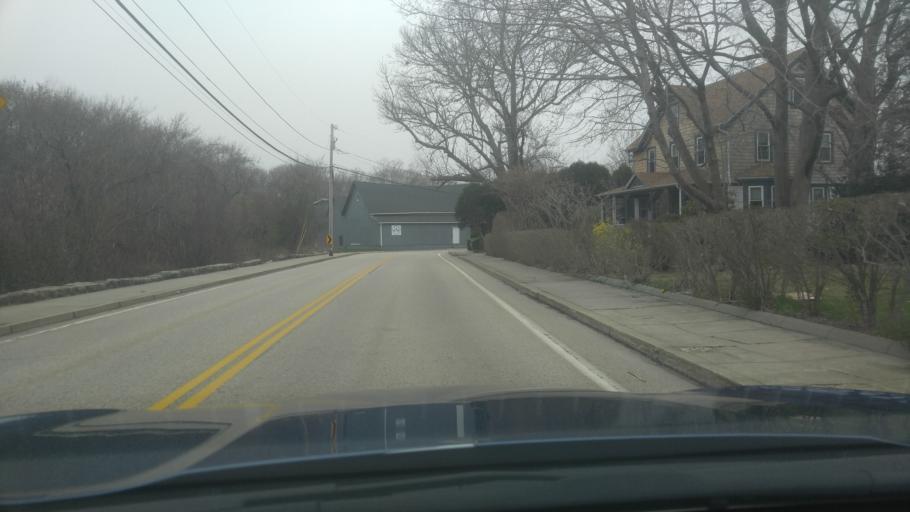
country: US
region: Rhode Island
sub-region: Washington County
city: Narragansett Pier
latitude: 41.4322
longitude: -71.4656
